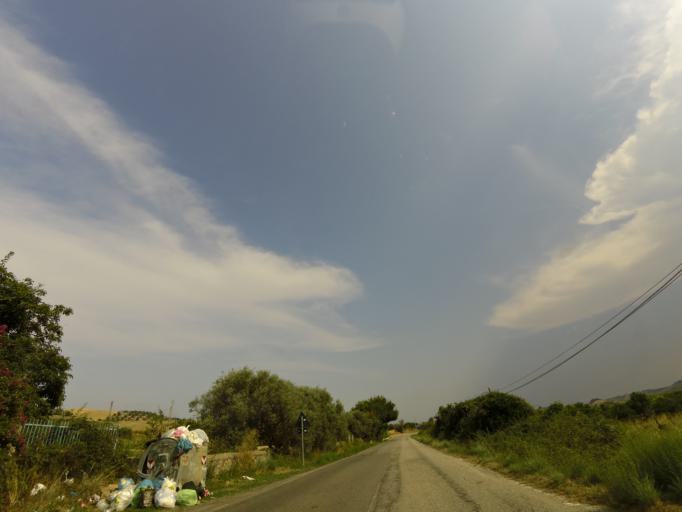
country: IT
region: Calabria
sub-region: Provincia di Reggio Calabria
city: Monasterace
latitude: 38.4489
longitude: 16.5325
